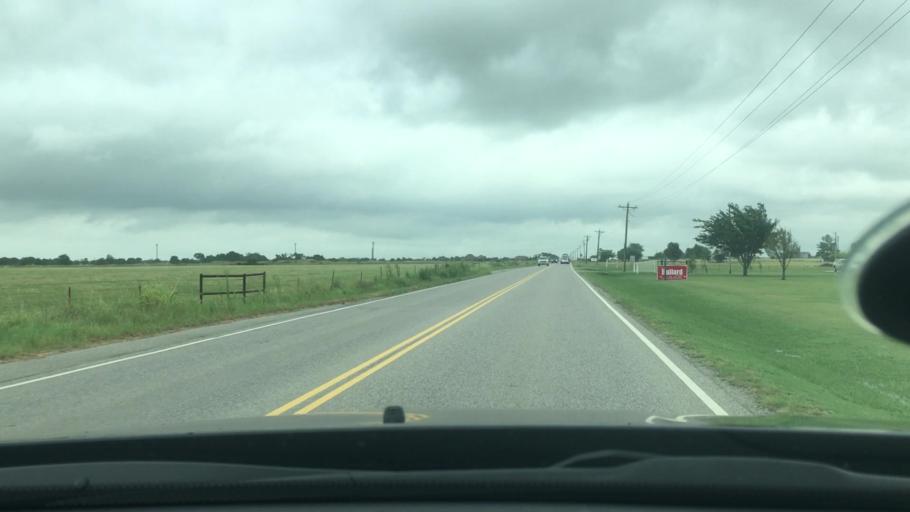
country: US
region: Oklahoma
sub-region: Bryan County
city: Colbert
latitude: 33.9076
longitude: -96.5006
